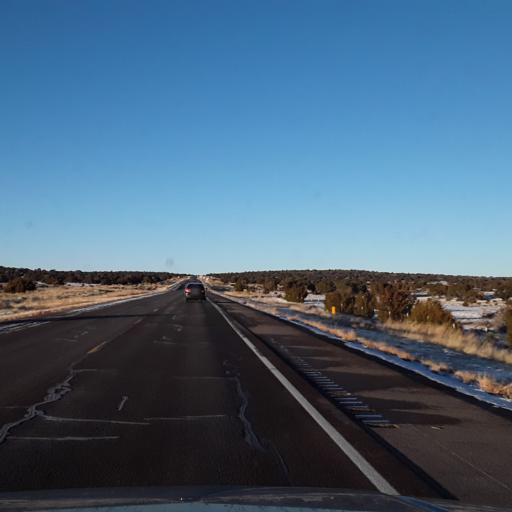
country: US
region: New Mexico
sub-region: Lincoln County
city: Carrizozo
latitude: 34.2040
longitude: -105.6486
